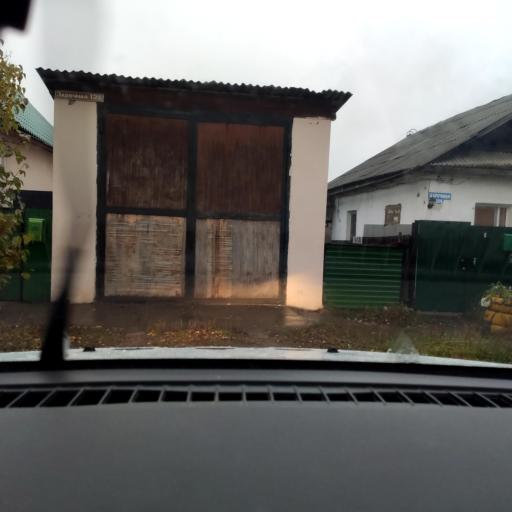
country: RU
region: Perm
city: Kondratovo
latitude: 58.0496
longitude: 56.0961
